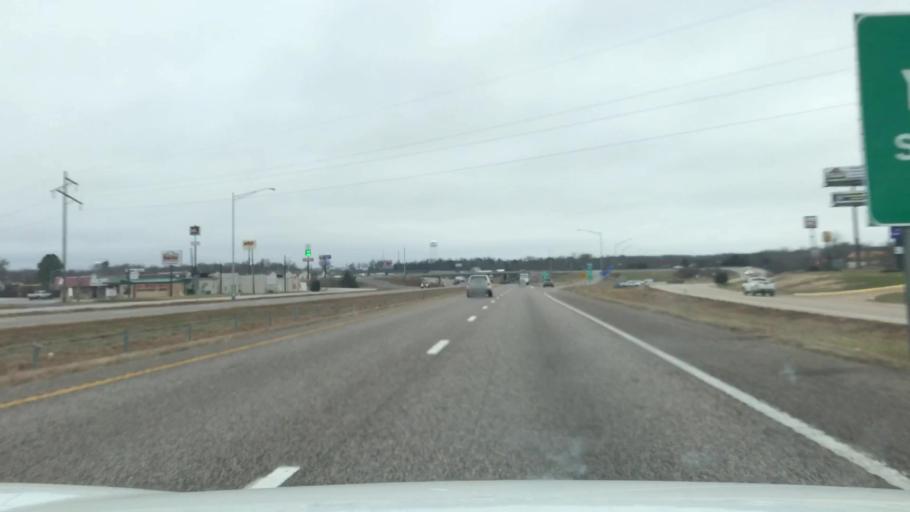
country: US
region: Missouri
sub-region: Franklin County
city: Sullivan
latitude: 38.2150
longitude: -91.1686
